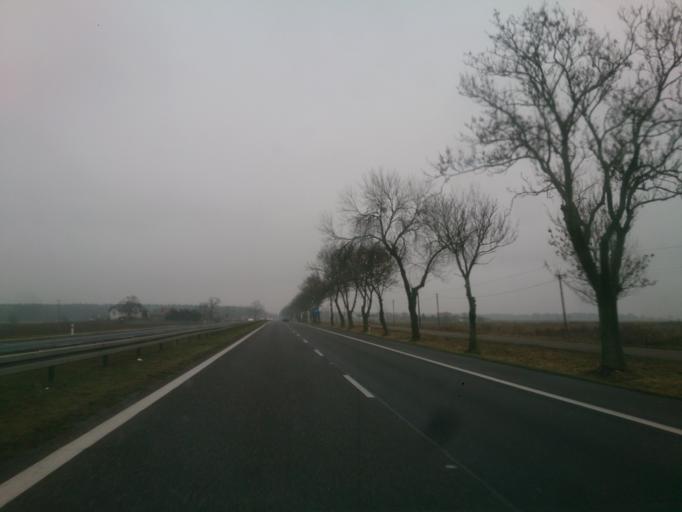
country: PL
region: Masovian Voivodeship
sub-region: Powiat nowodworski
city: Zakroczym
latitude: 52.4676
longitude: 20.5708
